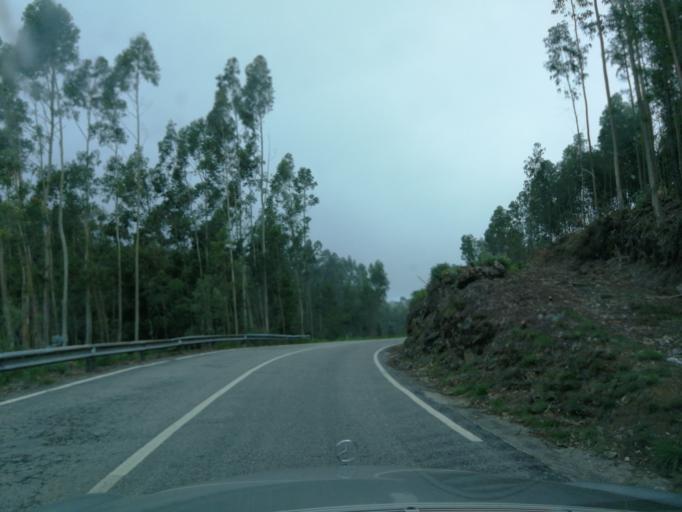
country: PT
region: Braga
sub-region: Braga
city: Braga
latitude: 41.5183
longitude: -8.3792
